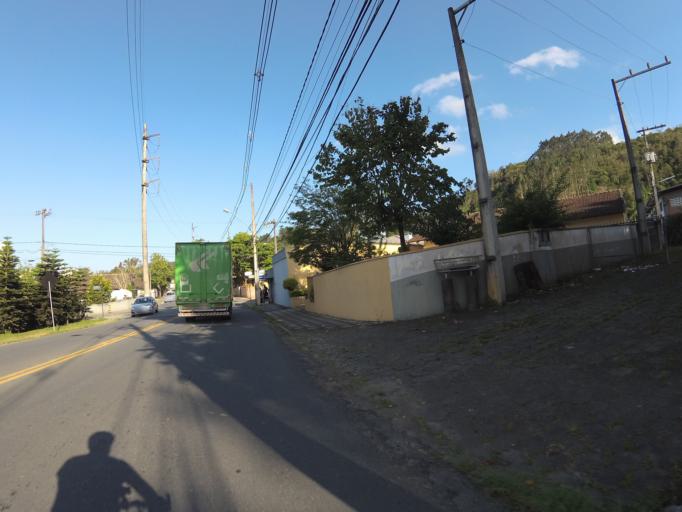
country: BR
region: Santa Catarina
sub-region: Blumenau
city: Blumenau
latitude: -26.9240
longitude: -49.1080
